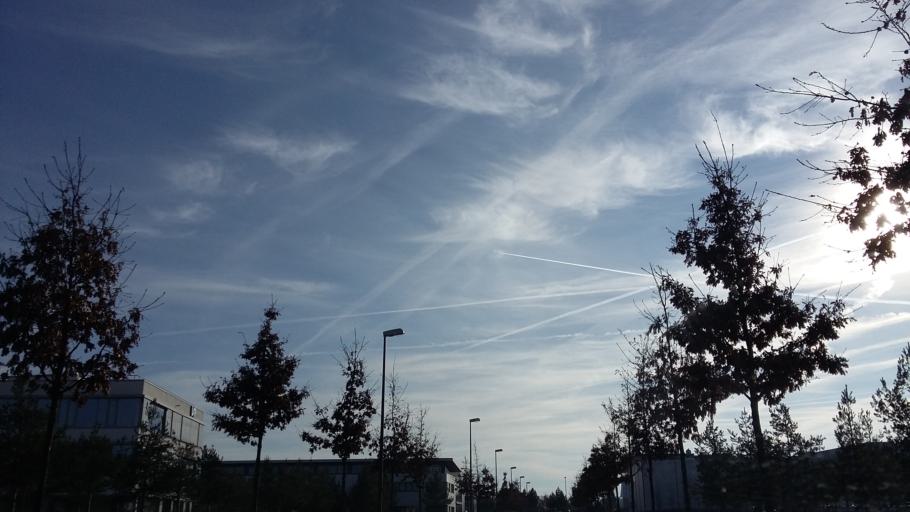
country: DE
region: Bavaria
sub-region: Upper Bavaria
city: Grafelfing
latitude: 48.1371
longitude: 11.4129
